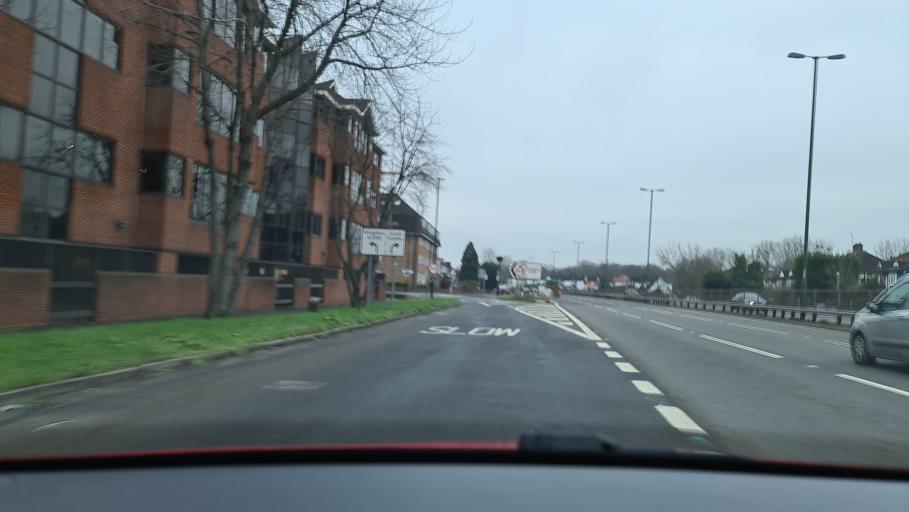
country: GB
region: England
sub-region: Greater London
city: New Malden
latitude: 51.4150
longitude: -0.2504
